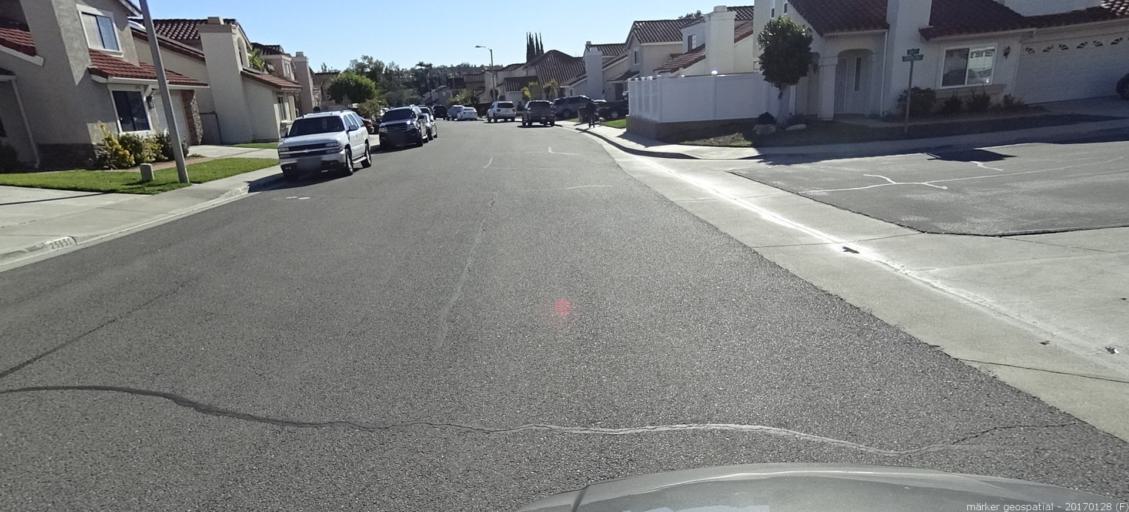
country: US
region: California
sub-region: Orange County
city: Lake Forest
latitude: 33.6519
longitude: -117.6784
